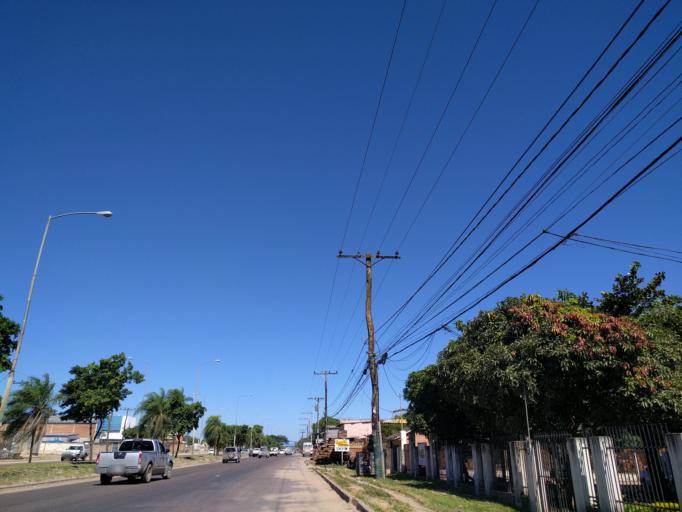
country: BO
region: Santa Cruz
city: Santa Cruz de la Sierra
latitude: -17.8327
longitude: -63.2319
